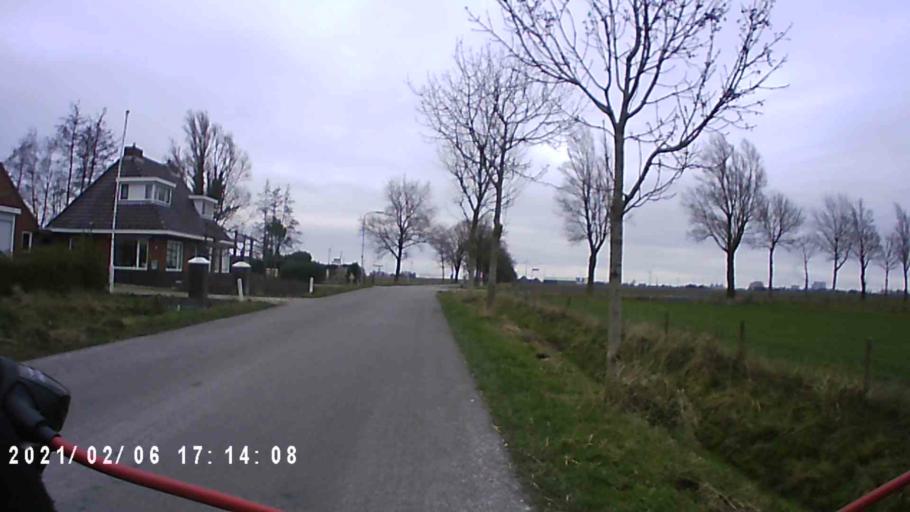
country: NL
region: Groningen
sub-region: Gemeente Appingedam
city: Appingedam
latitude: 53.4242
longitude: 6.7749
